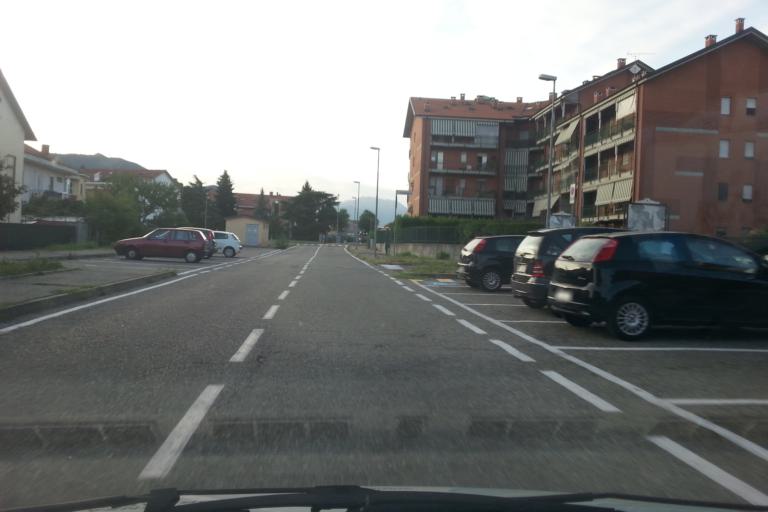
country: IT
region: Piedmont
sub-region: Provincia di Torino
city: Piossasco
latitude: 44.9909
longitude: 7.4740
